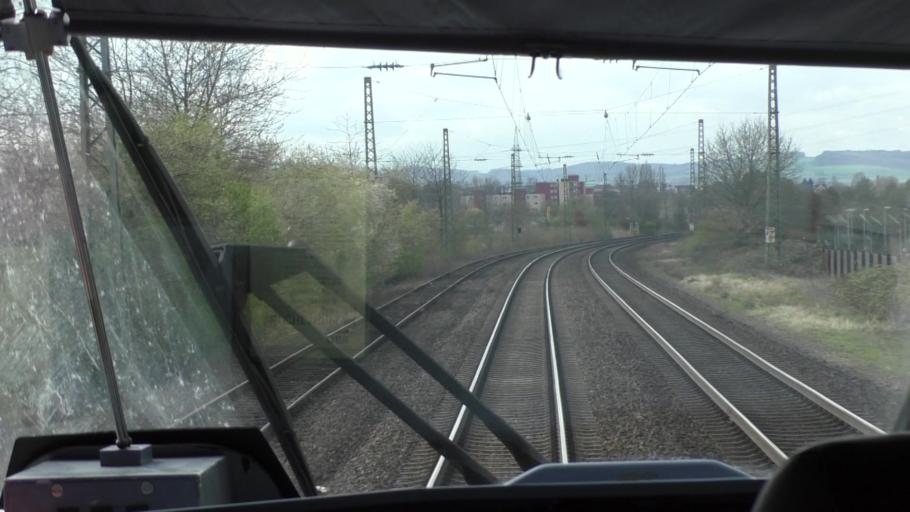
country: DE
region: Rheinland-Pfalz
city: Kettig
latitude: 50.4066
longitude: 7.4852
